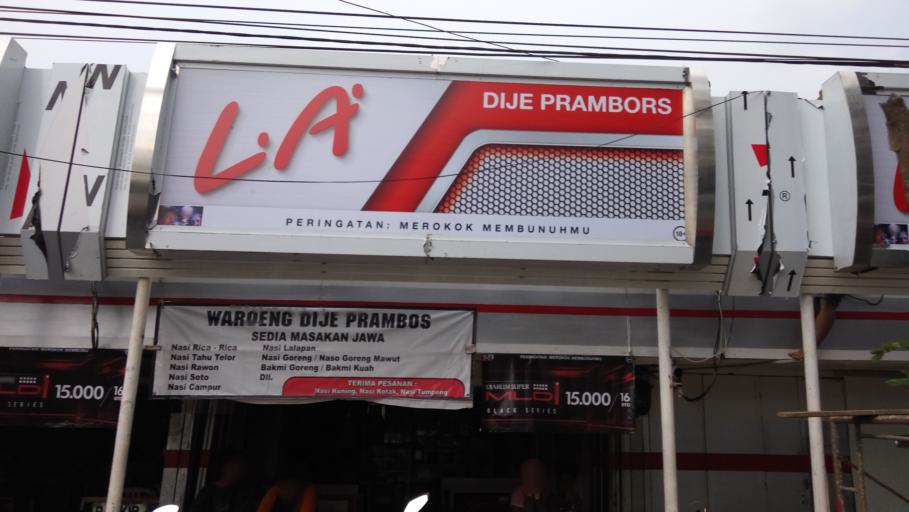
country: ID
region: East Java
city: Malang
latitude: -7.9228
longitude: 112.5962
